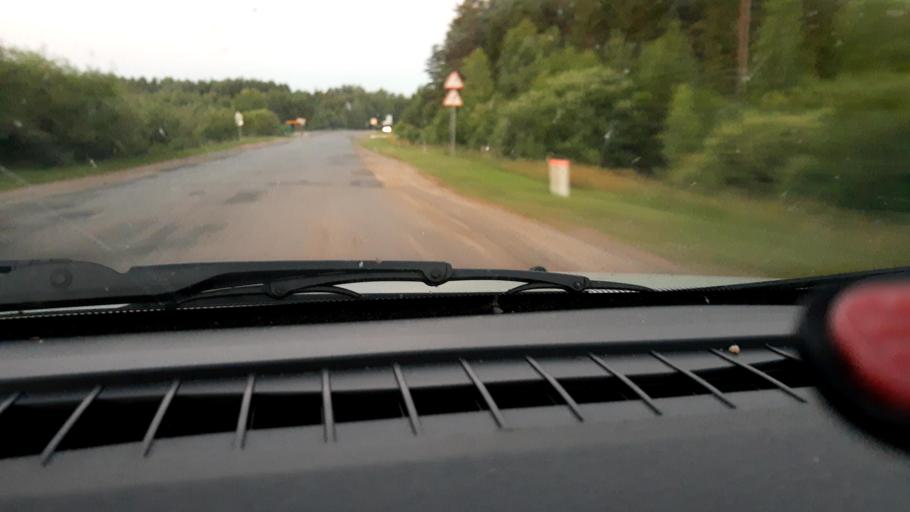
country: RU
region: Nizjnij Novgorod
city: Uren'
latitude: 57.4824
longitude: 46.0289
